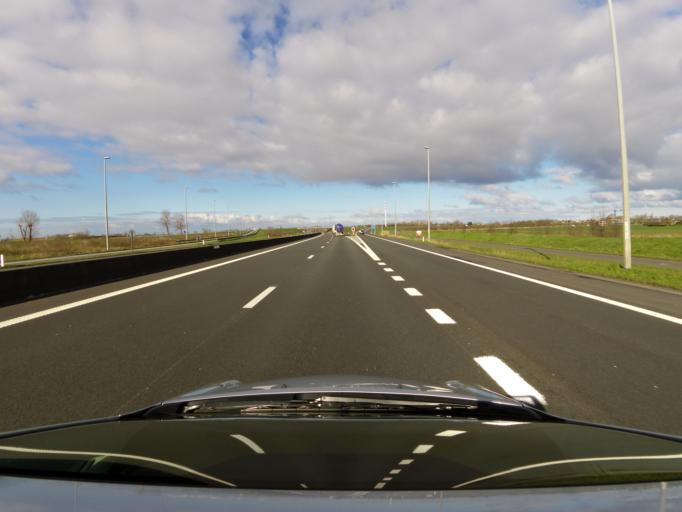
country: BE
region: Flanders
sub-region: Provincie West-Vlaanderen
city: De Panne
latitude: 51.0686
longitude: 2.6106
